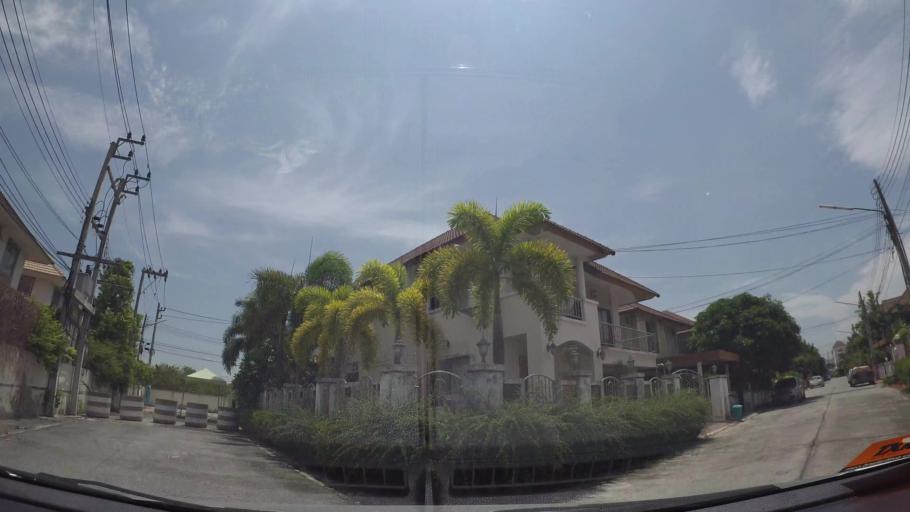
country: TH
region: Chon Buri
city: Chon Buri
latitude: 13.3297
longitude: 100.9439
